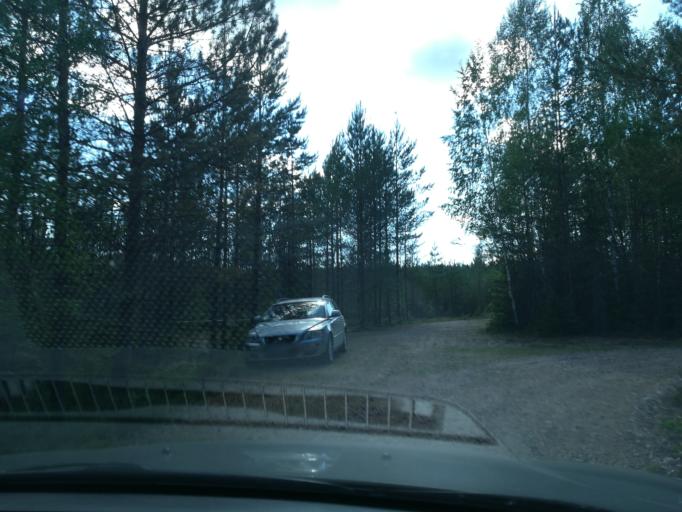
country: FI
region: South Karelia
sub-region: Imatra
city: Ruokolahti
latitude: 61.5375
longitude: 28.8149
